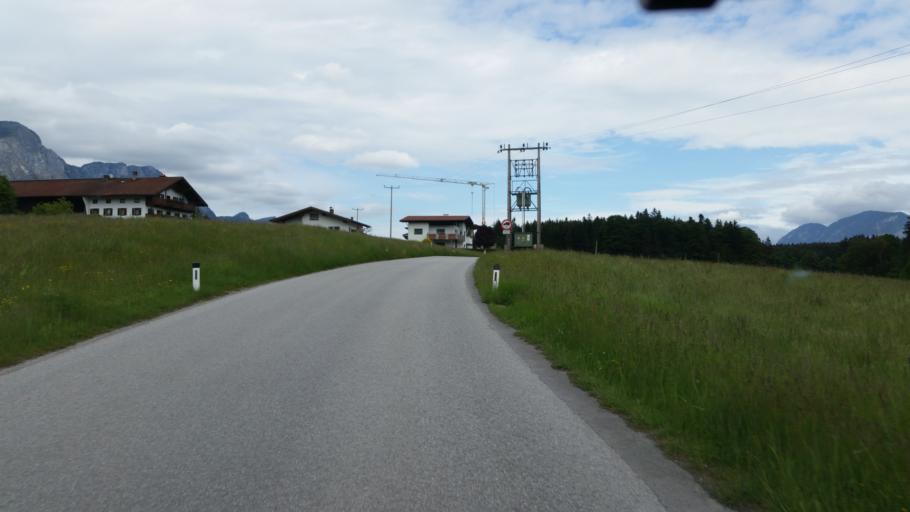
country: AT
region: Tyrol
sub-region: Politischer Bezirk Kufstein
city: Kundl
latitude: 47.4937
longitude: 12.0122
